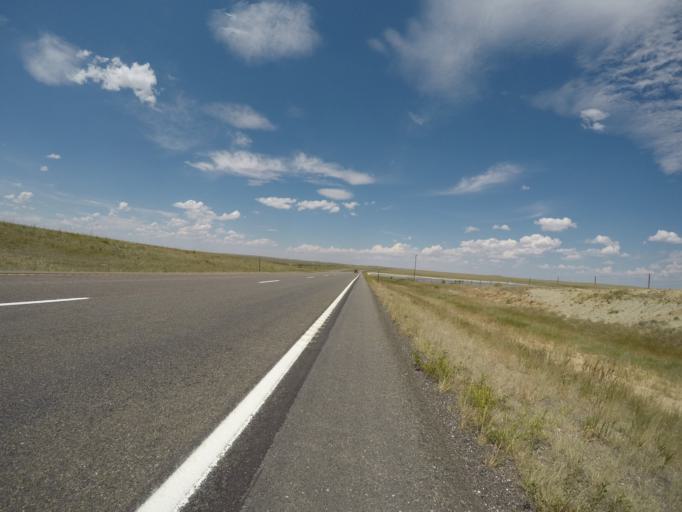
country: US
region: Wyoming
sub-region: Albany County
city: Laramie
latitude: 41.6346
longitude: -105.7682
